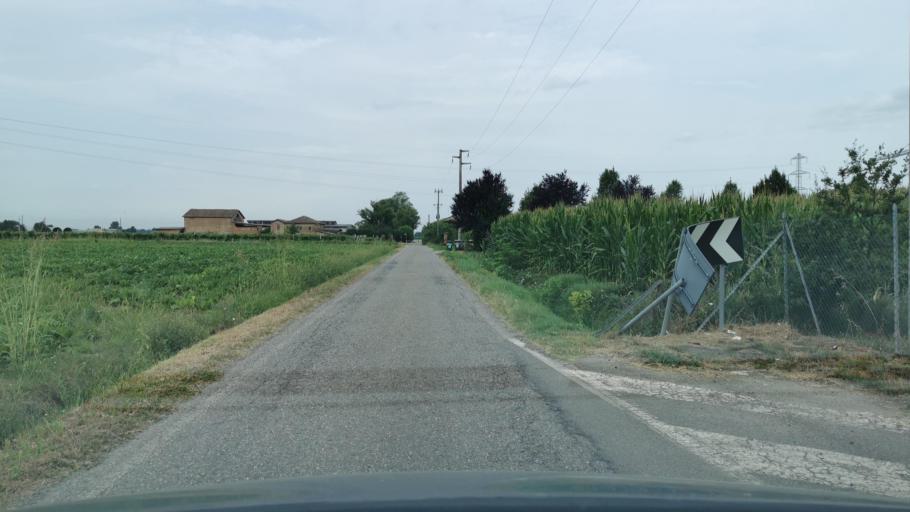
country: IT
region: Emilia-Romagna
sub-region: Provincia di Modena
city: Villanova
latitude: 44.6968
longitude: 10.8890
